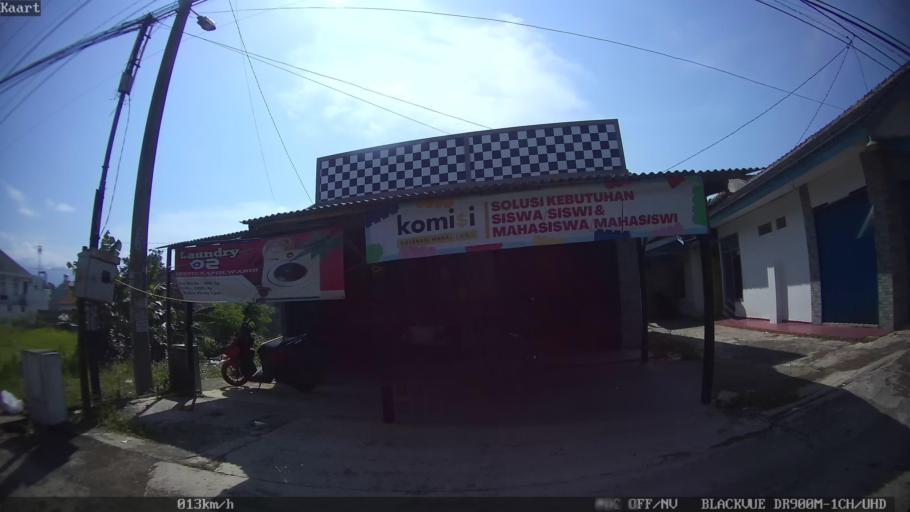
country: ID
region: Lampung
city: Kedaton
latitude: -5.3703
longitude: 105.2470
